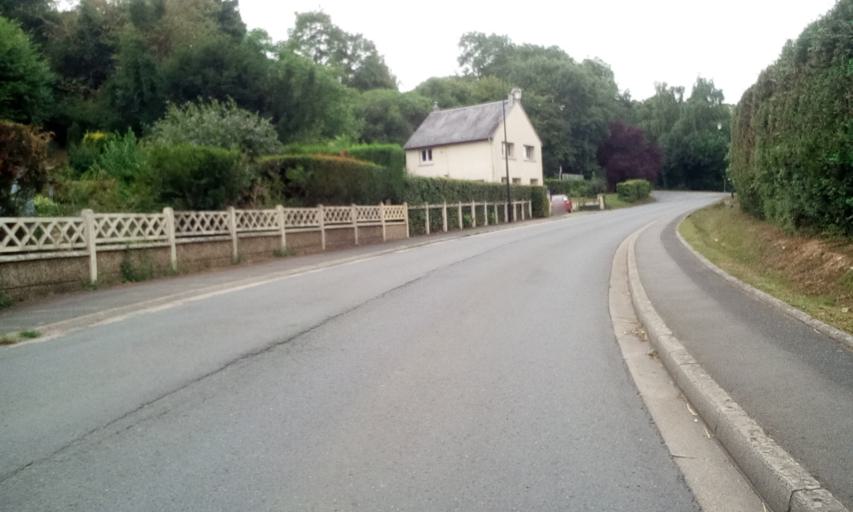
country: FR
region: Lower Normandy
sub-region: Departement du Calvados
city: Verson
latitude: 49.1523
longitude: -0.4461
